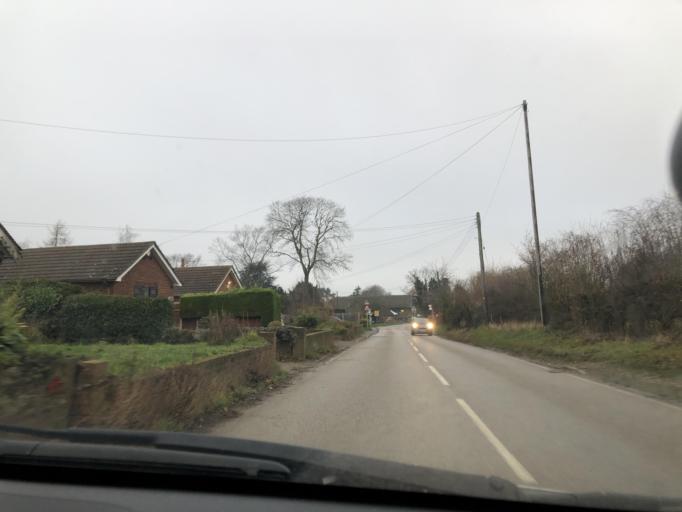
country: GB
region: England
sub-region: Kent
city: Longfield
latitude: 51.4115
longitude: 0.3298
